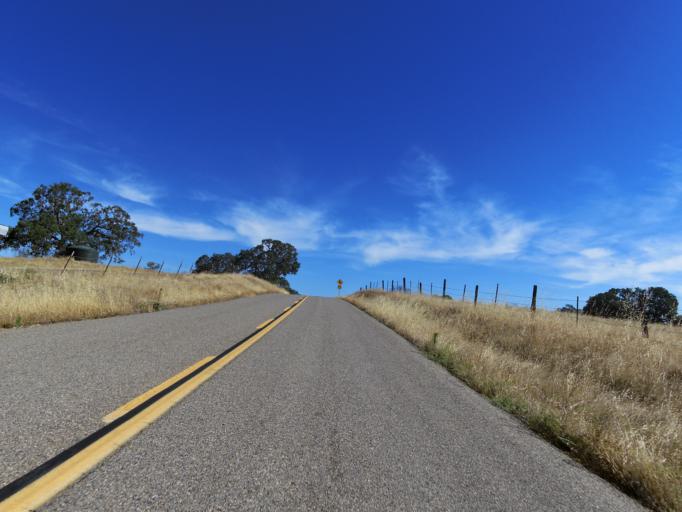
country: US
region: California
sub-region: Madera County
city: Yosemite Lakes
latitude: 37.2580
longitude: -119.9249
